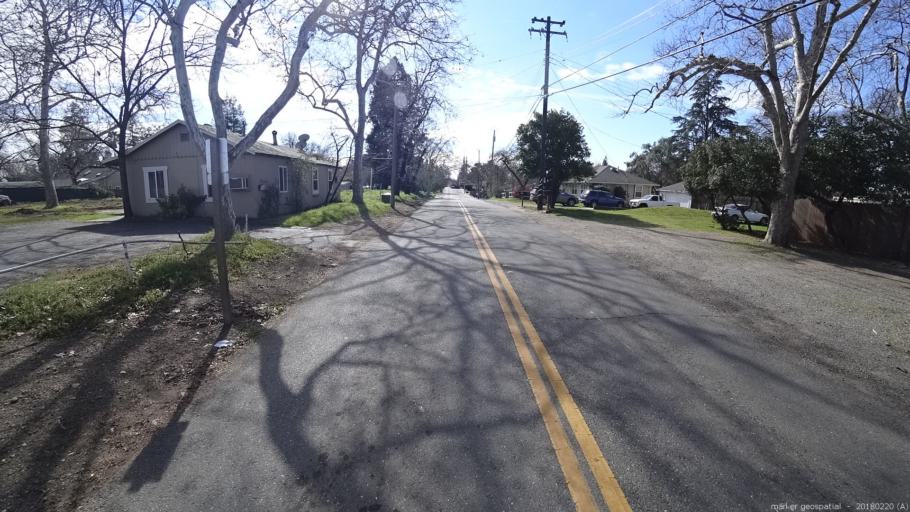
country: US
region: California
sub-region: Sacramento County
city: Orangevale
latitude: 38.6780
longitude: -121.2163
